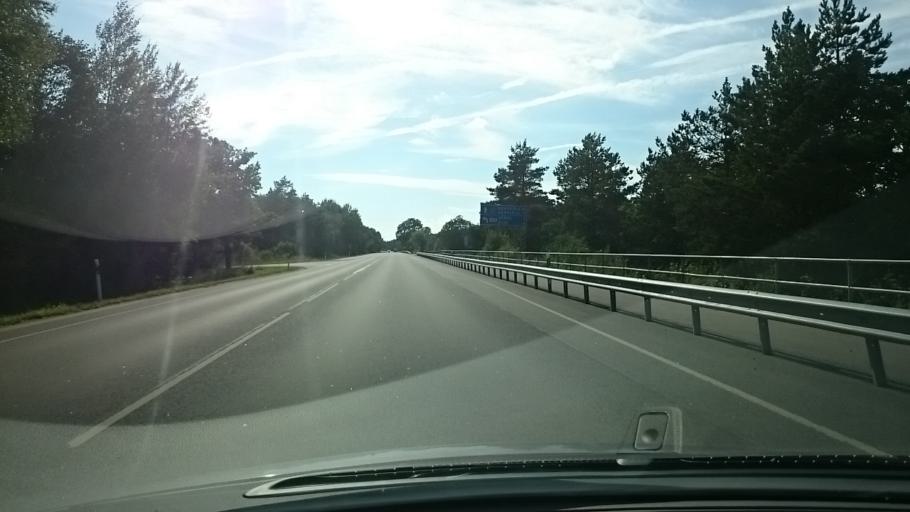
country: EE
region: Laeaene
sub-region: Ridala Parish
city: Uuemoisa
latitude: 58.9487
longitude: 23.6291
